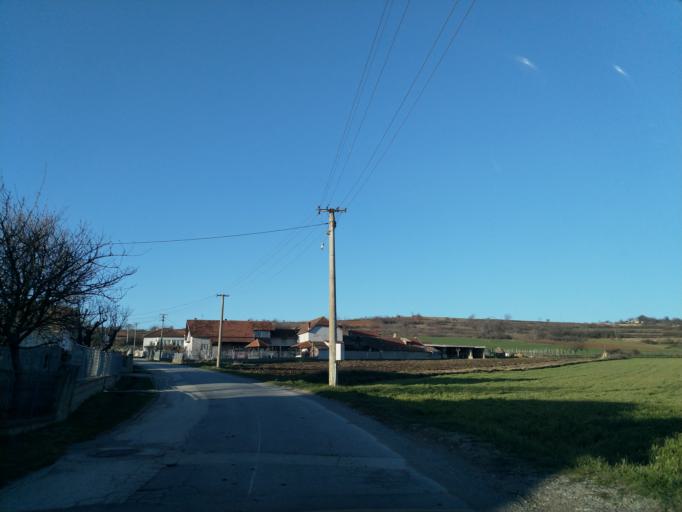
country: RS
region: Central Serbia
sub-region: Pomoravski Okrug
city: Paracin
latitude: 43.9200
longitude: 21.5108
